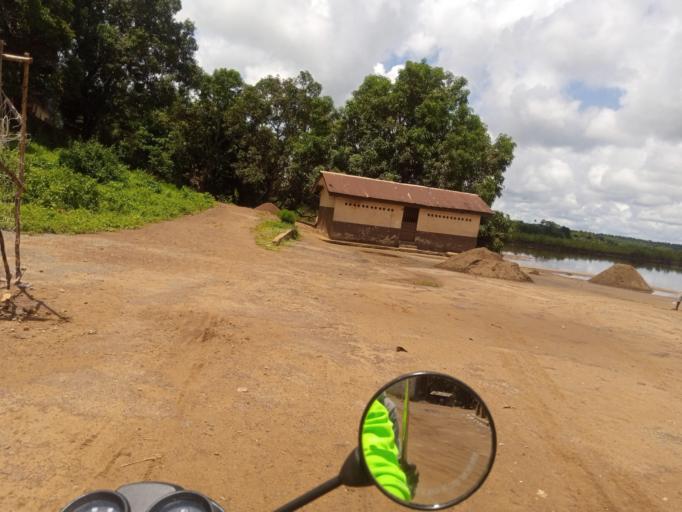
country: SL
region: Northern Province
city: Port Loko
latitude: 8.7630
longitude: -12.7919
